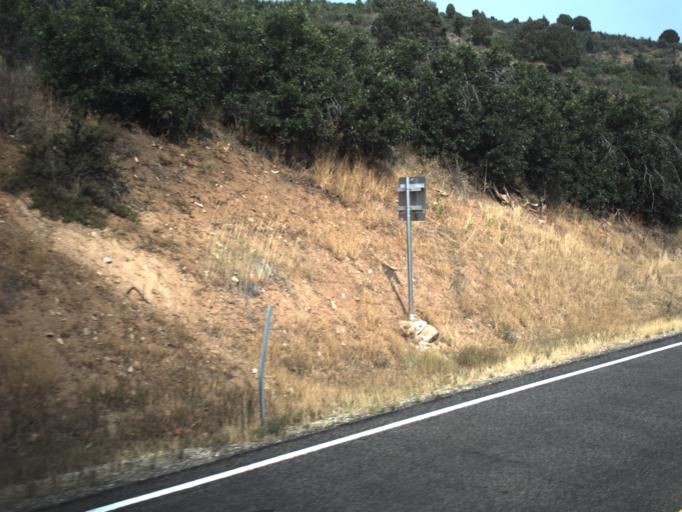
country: US
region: Utah
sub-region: Summit County
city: Francis
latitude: 40.6247
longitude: -111.2272
